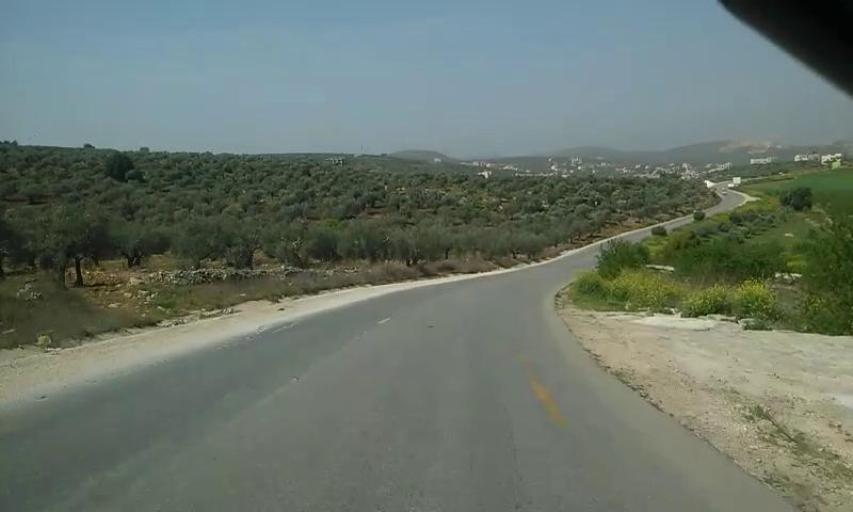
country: PS
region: West Bank
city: Az Zababidah
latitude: 32.3755
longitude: 35.3352
